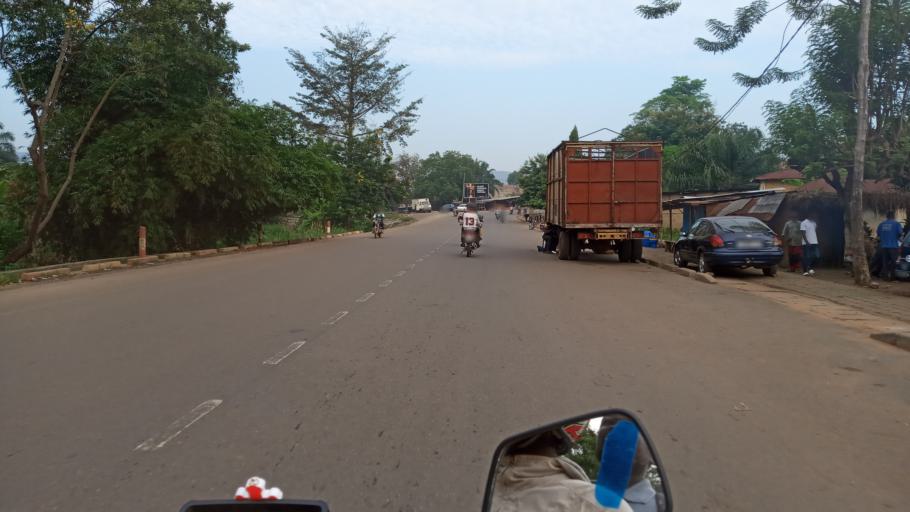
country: TG
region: Plateaux
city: Kpalime
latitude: 6.9036
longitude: 0.6324
